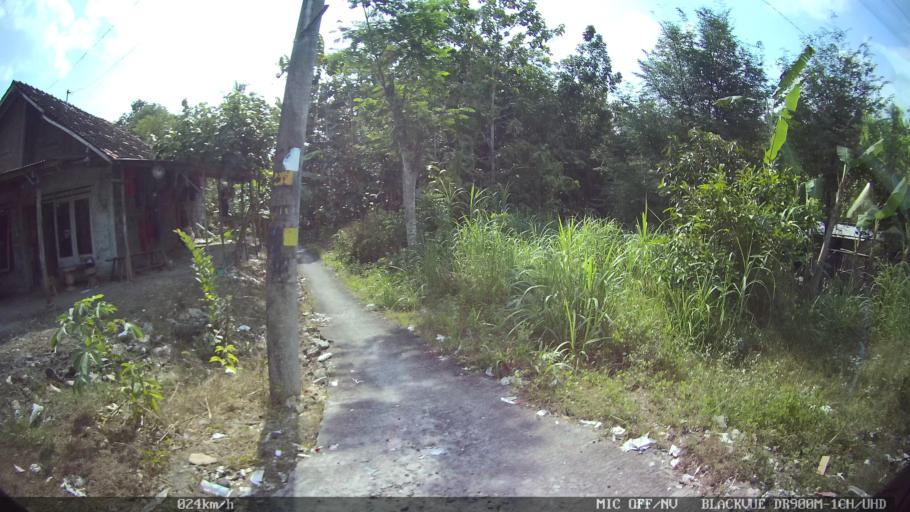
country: ID
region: Daerah Istimewa Yogyakarta
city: Kasihan
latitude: -7.8470
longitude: 110.3007
